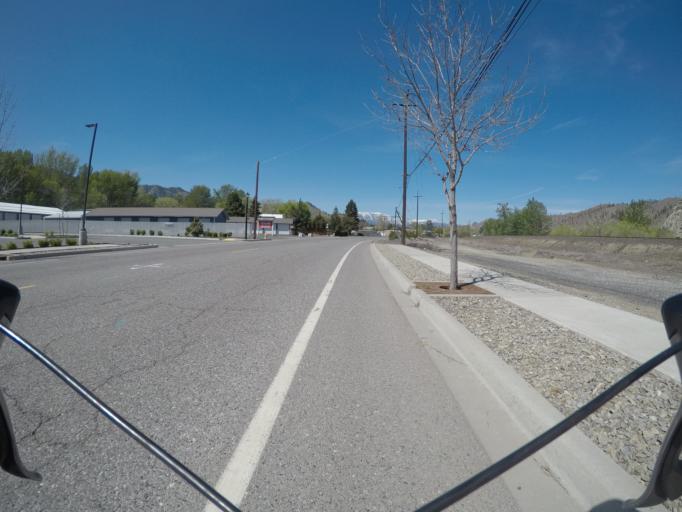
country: US
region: Washington
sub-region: Chelan County
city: Cashmere
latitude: 47.5221
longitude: -120.4808
